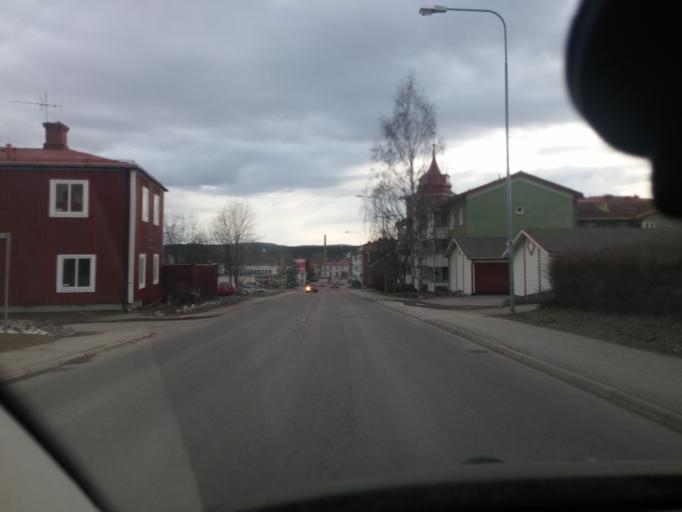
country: SE
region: Gaevleborg
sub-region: Ljusdals Kommun
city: Ljusdal
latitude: 61.8307
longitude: 16.0939
